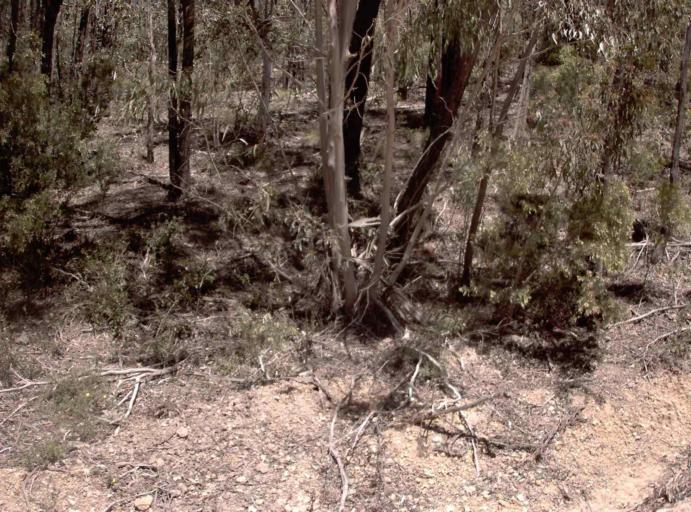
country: AU
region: New South Wales
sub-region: Snowy River
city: Jindabyne
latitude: -37.0776
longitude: 148.3293
